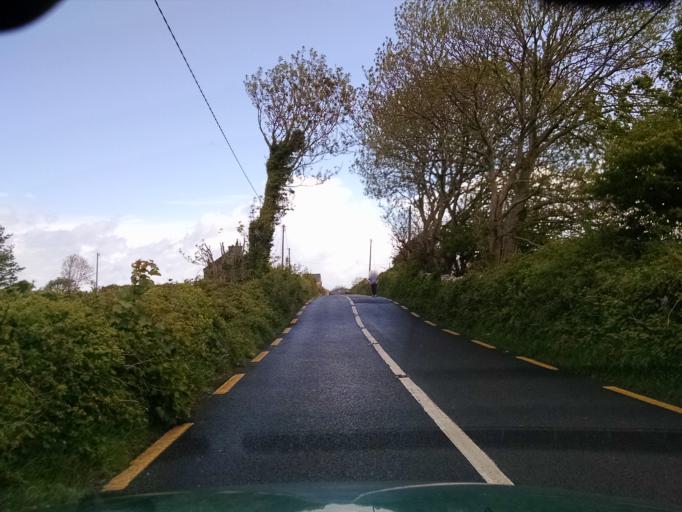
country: IE
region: Connaught
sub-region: County Galway
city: Bearna
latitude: 53.1022
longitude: -9.1622
